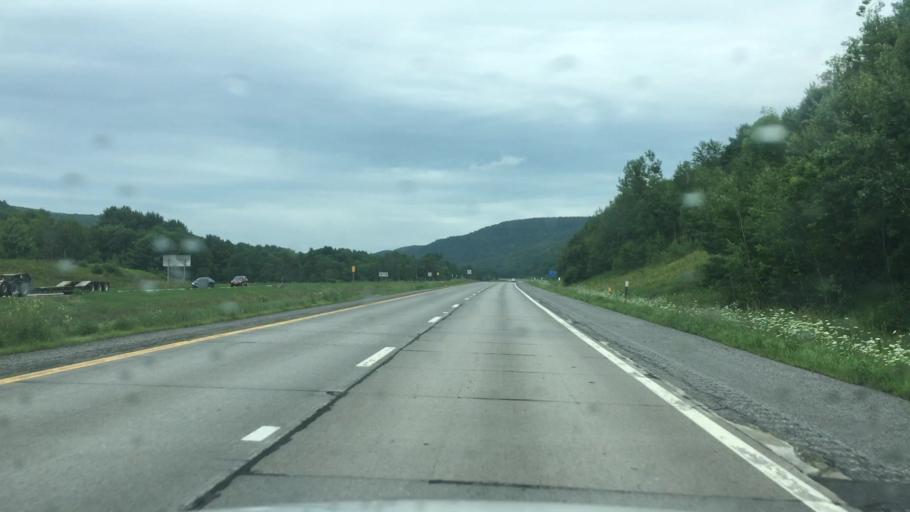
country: US
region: New York
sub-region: Otsego County
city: Worcester
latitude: 42.5501
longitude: -74.8026
